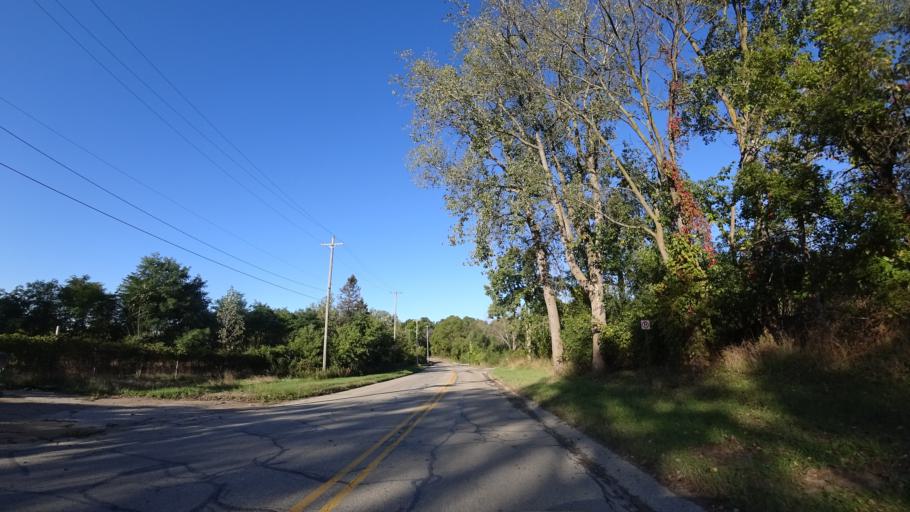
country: US
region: Michigan
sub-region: Kent County
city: Wyoming
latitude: 42.9463
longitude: -85.7224
